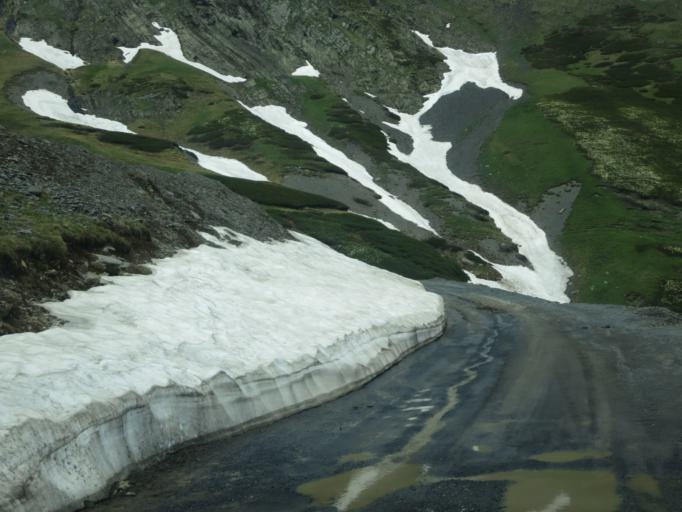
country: GE
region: Kakheti
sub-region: Telavi
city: Telavi
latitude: 42.2852
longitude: 45.5108
